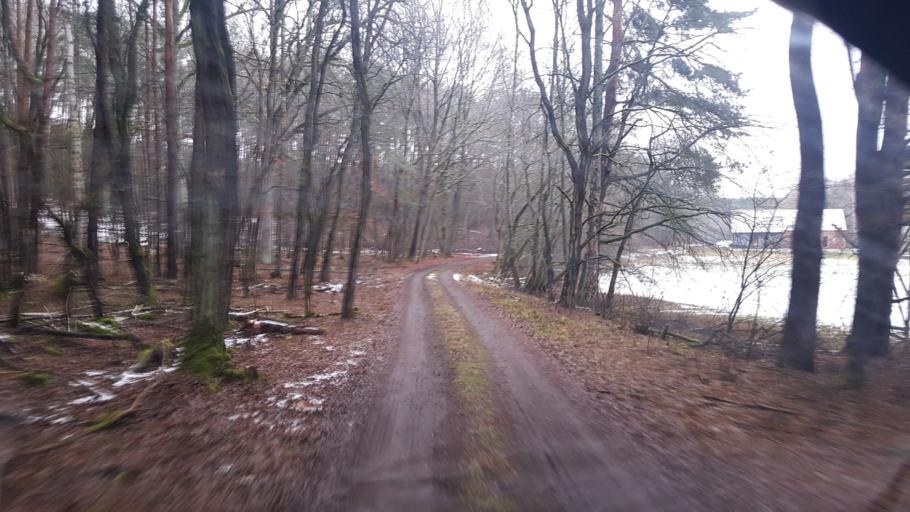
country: DE
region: Brandenburg
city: Jamlitz
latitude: 51.9954
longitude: 14.3567
